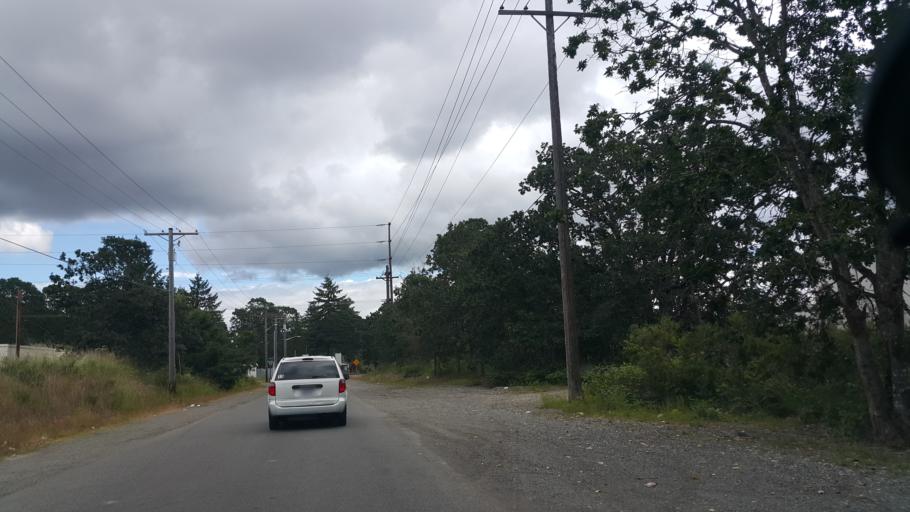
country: US
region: Washington
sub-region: Pierce County
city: McChord Air Force Base
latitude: 47.1394
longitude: -122.5006
